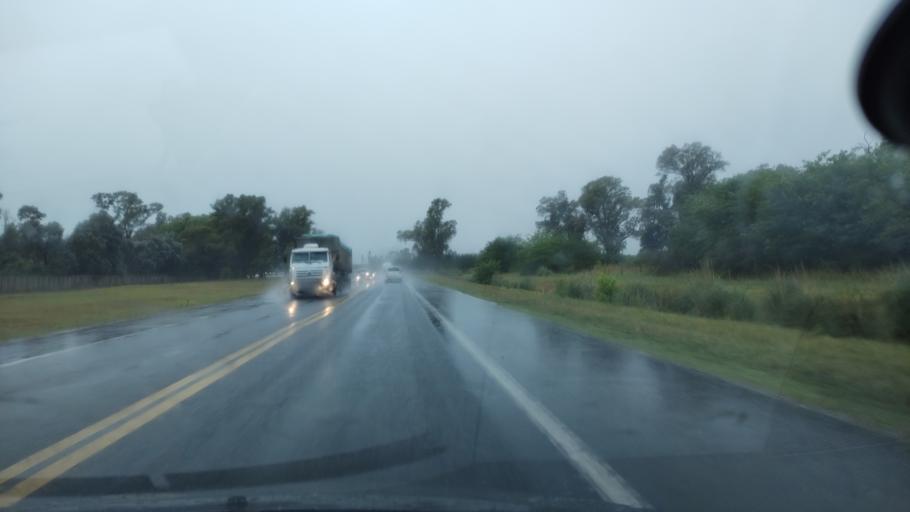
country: AR
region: Buenos Aires
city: Canuelas
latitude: -35.0538
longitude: -58.7800
